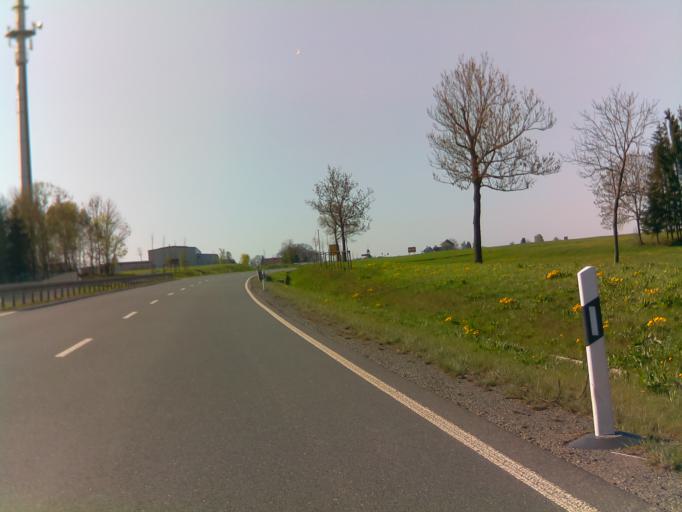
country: DE
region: Thuringia
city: Dittersdorf
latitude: 50.6536
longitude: 11.8157
